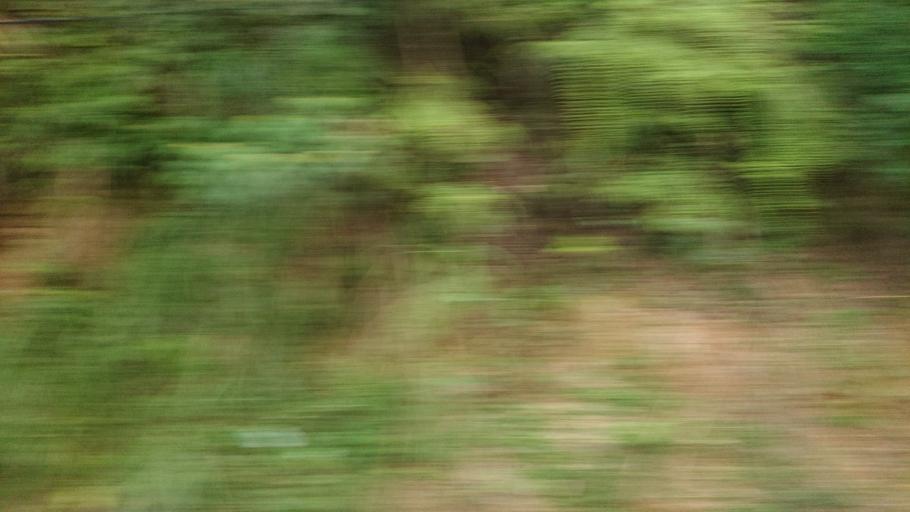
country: TW
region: Taiwan
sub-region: Nantou
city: Puli
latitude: 23.9759
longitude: 120.9892
